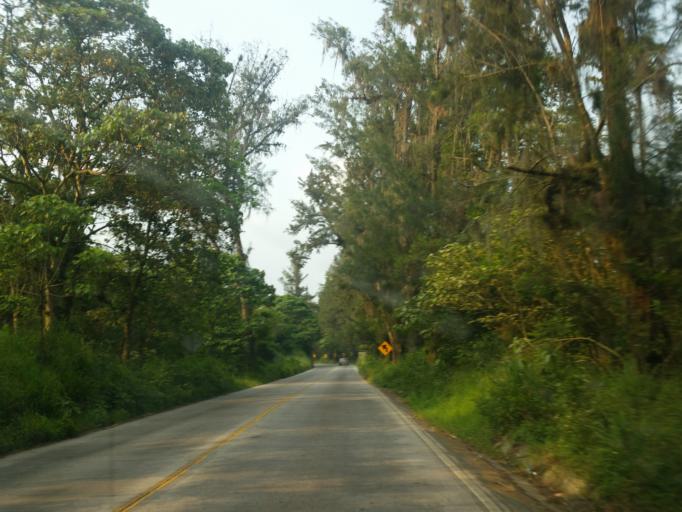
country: MX
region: Veracruz
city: Coatepec
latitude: 19.4342
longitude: -96.9555
